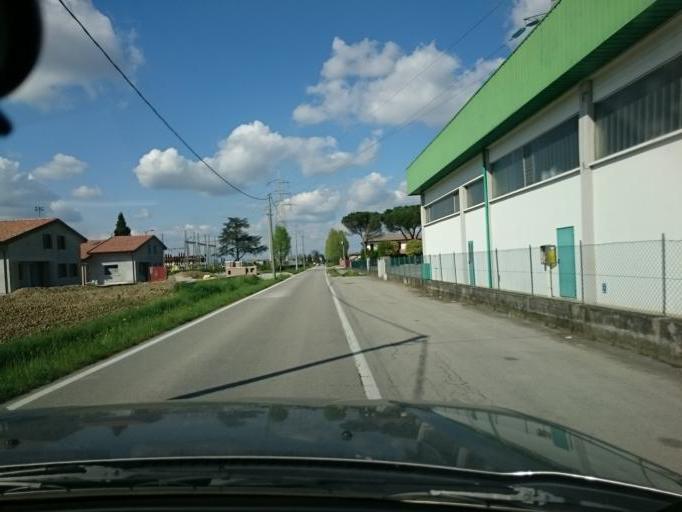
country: IT
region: Veneto
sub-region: Provincia di Padova
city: Villanova
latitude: 45.4816
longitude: 11.9838
